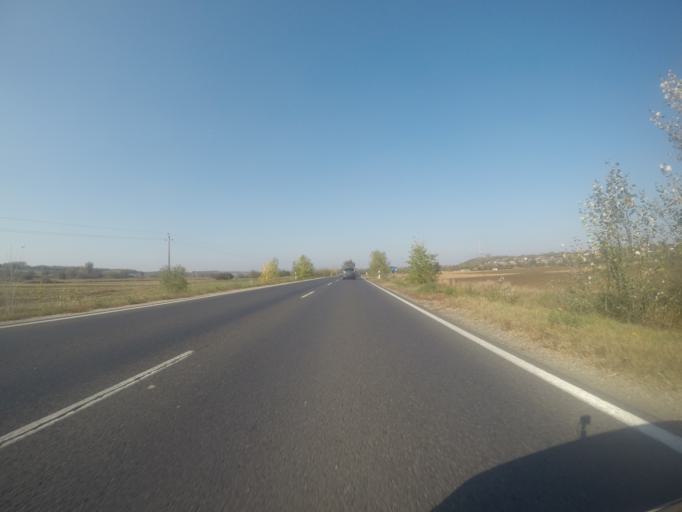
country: HU
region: Tolna
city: Dunafoldvar
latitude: 46.8174
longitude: 18.9069
